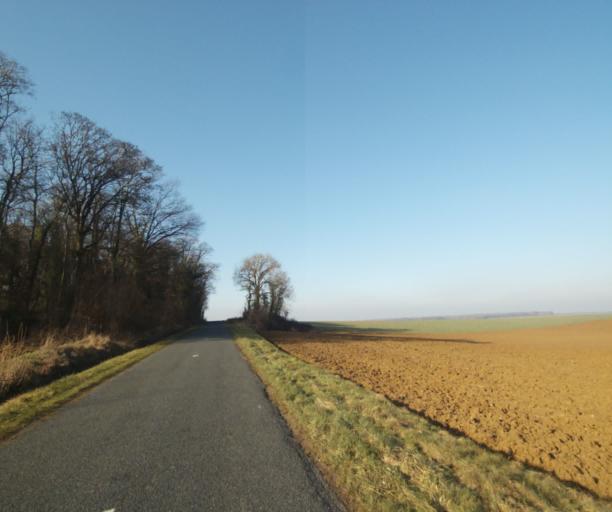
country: FR
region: Champagne-Ardenne
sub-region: Departement de la Haute-Marne
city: Chevillon
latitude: 48.4884
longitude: 5.0796
